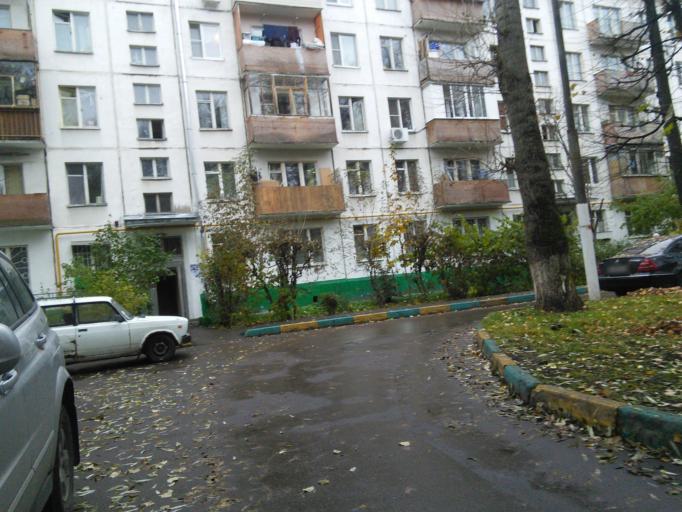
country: RU
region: Moscow
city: Tsaritsyno
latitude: 55.6335
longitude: 37.6541
